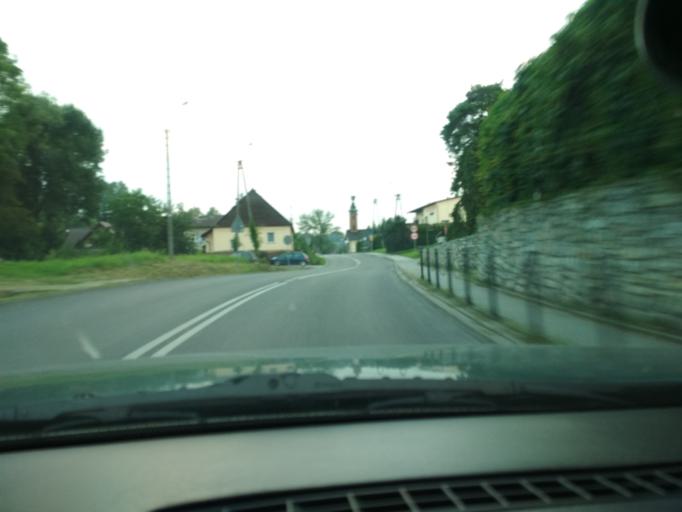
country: PL
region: Silesian Voivodeship
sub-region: Powiat bielski
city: Jasienica
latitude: 49.8431
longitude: 18.9414
